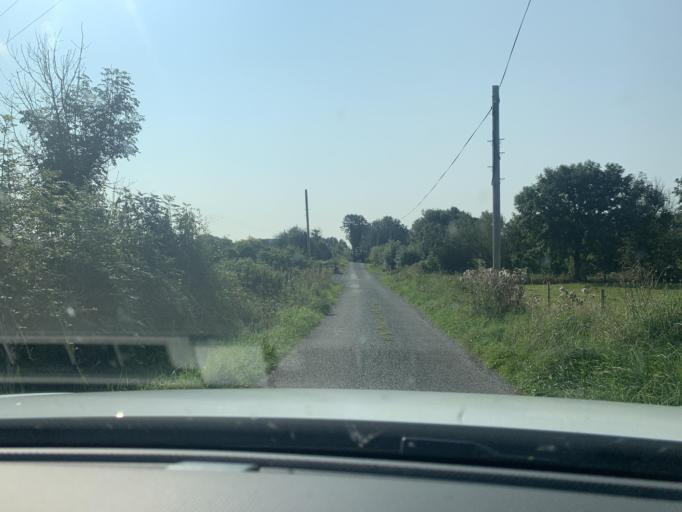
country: IE
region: Connaught
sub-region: Maigh Eo
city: Ballyhaunis
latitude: 53.8008
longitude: -8.7446
